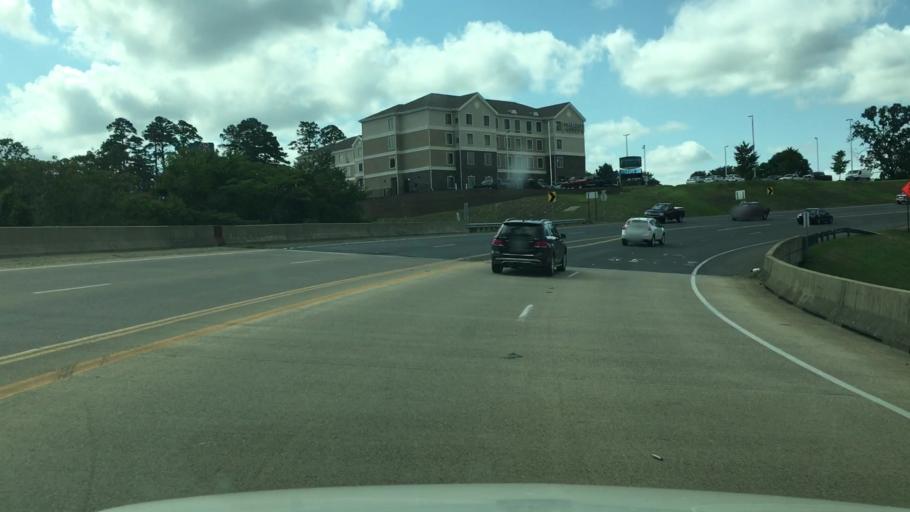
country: US
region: Arkansas
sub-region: Garland County
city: Lake Hamilton
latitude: 34.4295
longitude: -93.0849
